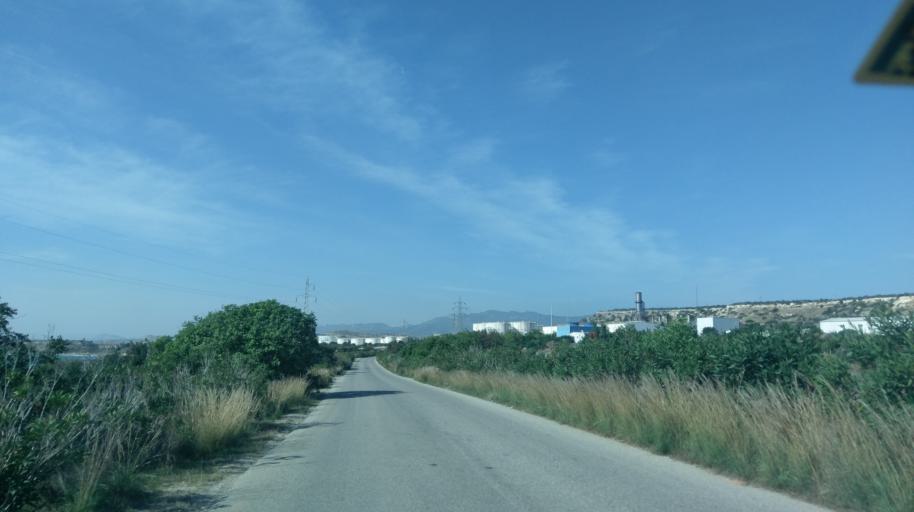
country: CY
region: Ammochostos
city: Trikomo
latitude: 35.3269
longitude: 34.0026
